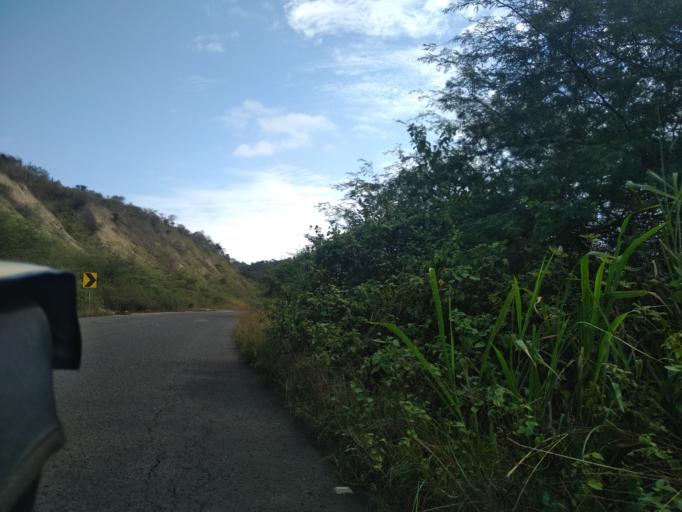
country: EC
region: Manabi
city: Jipijapa
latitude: -1.4347
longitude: -80.7537
